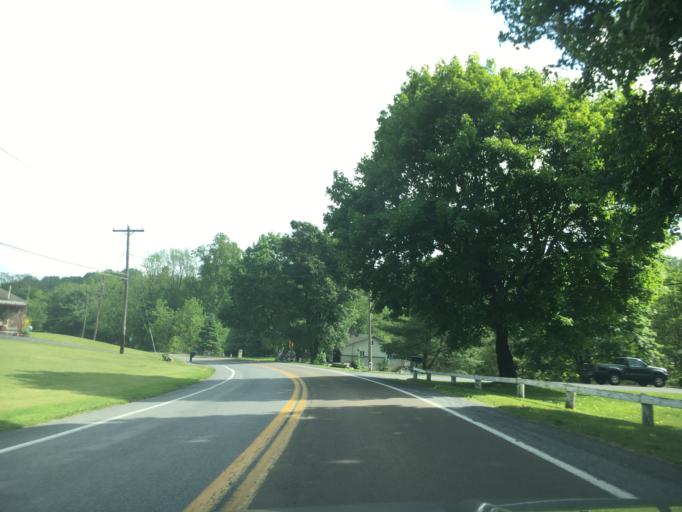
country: US
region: Pennsylvania
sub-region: Northampton County
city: Cherryville
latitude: 40.7448
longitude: -75.5494
